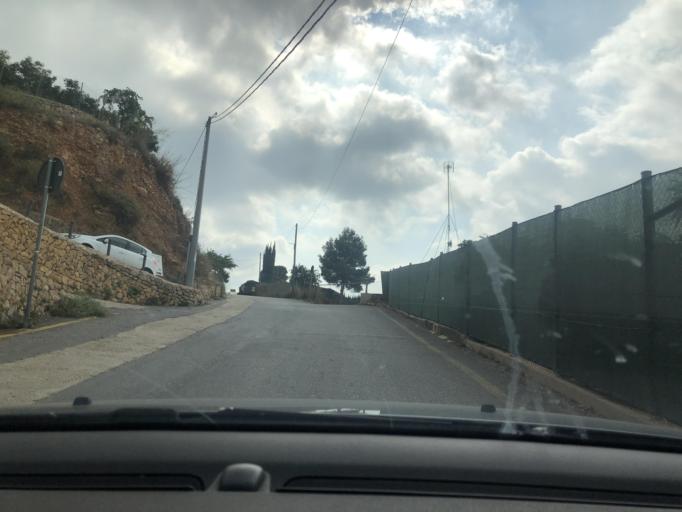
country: ES
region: Valencia
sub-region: Provincia de Alicante
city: Callosa d'En Sarria
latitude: 38.6587
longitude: -0.0958
